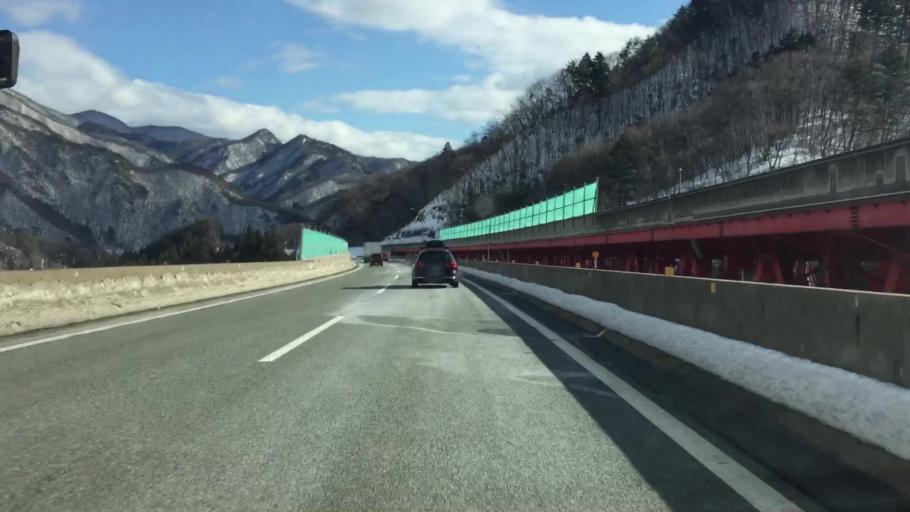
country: JP
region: Gunma
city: Numata
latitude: 36.7744
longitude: 138.9491
